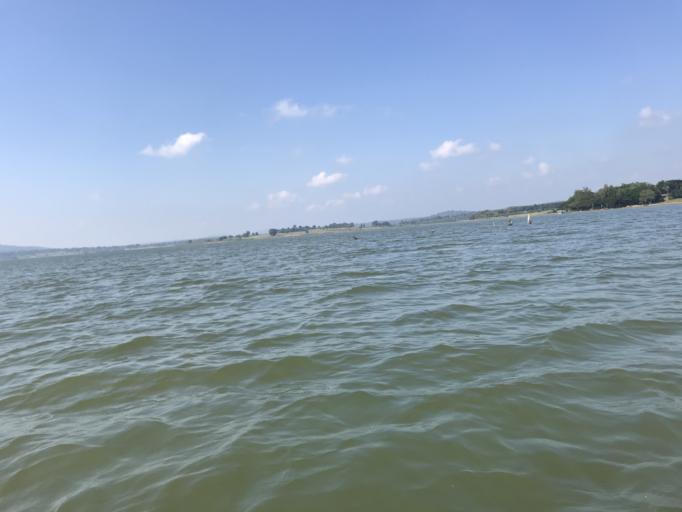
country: IN
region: Karnataka
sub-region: Mysore
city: Sargur
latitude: 11.9359
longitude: 76.2713
